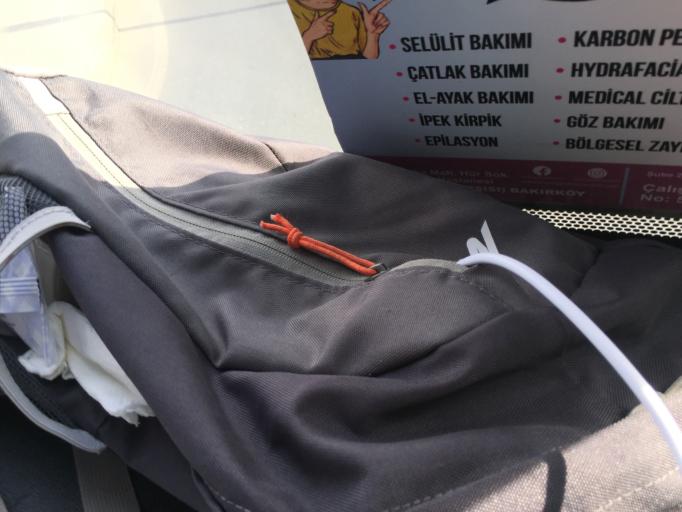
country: TR
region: Istanbul
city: Zeytinburnu
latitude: 40.9957
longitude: 28.9025
